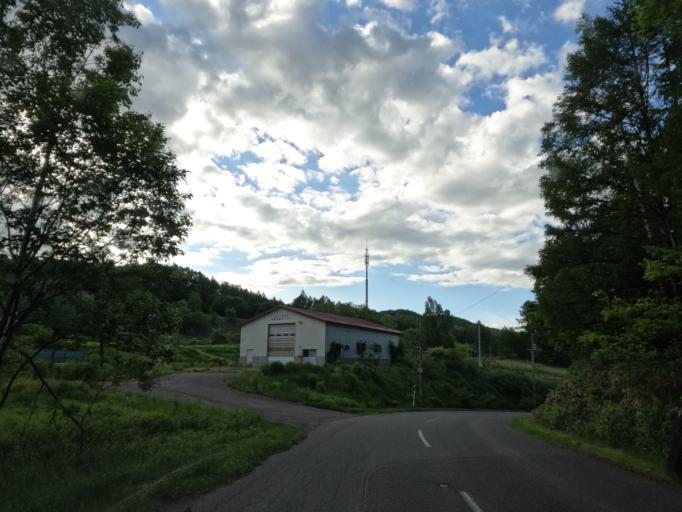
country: JP
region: Hokkaido
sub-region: Asahikawa-shi
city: Asahikawa
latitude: 43.8806
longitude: 142.4541
